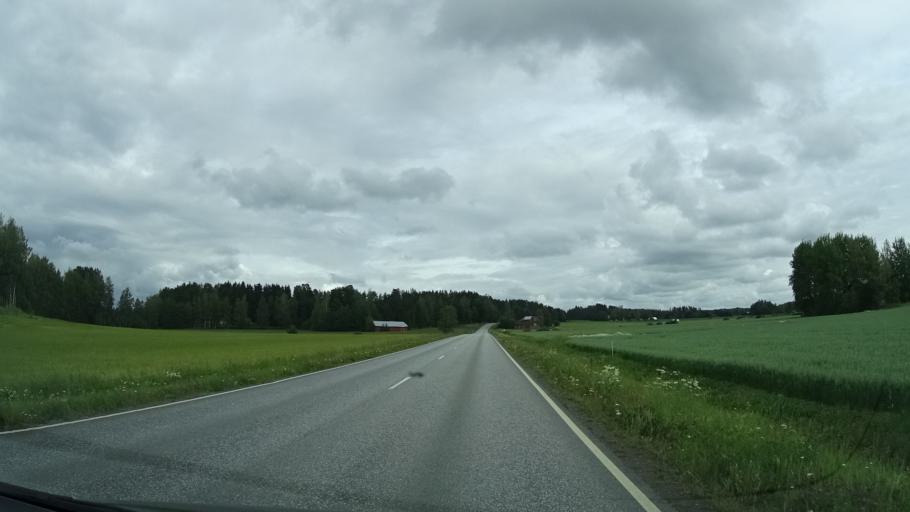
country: FI
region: Pirkanmaa
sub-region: Etelae-Pirkanmaa
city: Urjala
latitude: 61.0891
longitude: 23.4848
